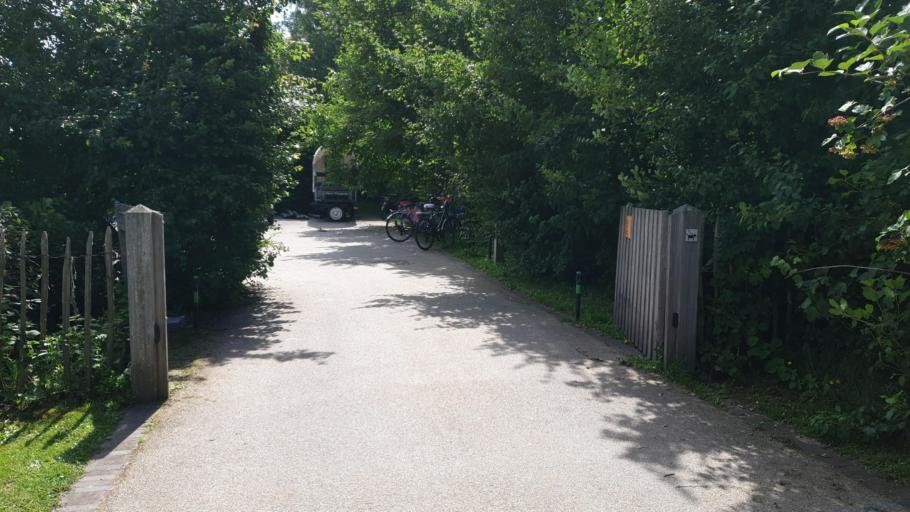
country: BE
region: Flanders
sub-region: Provincie West-Vlaanderen
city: Sint-Kruis
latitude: 51.2011
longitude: 3.2672
